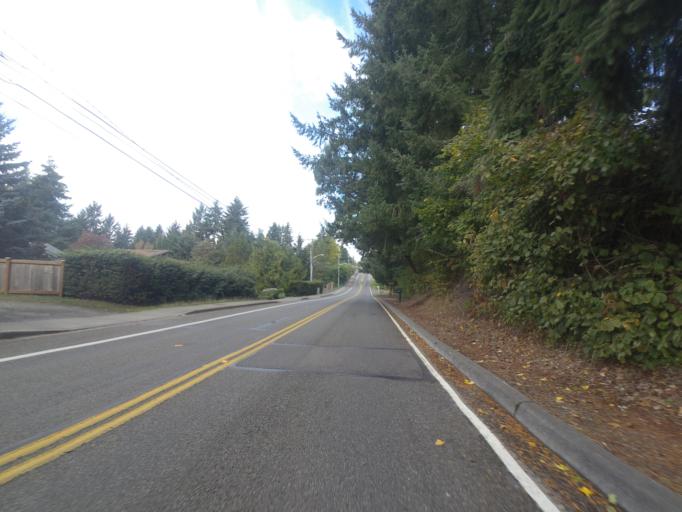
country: US
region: Washington
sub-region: Pierce County
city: University Place
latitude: 47.2234
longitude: -122.5450
